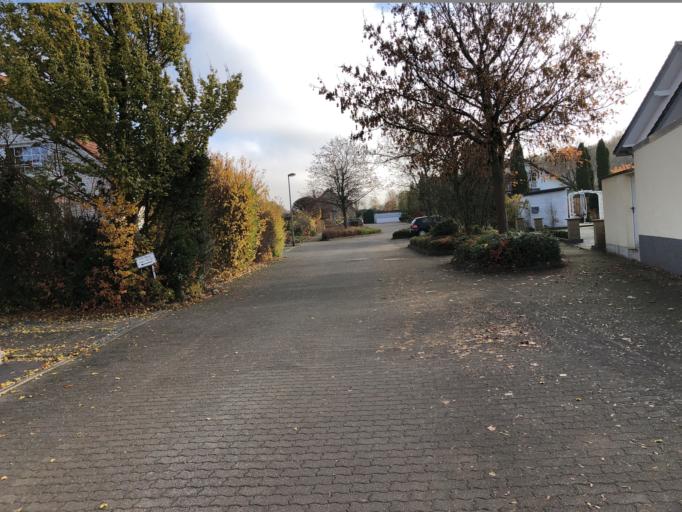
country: DE
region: North Rhine-Westphalia
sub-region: Regierungsbezirk Detmold
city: Detmold
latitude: 51.9308
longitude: 8.8479
